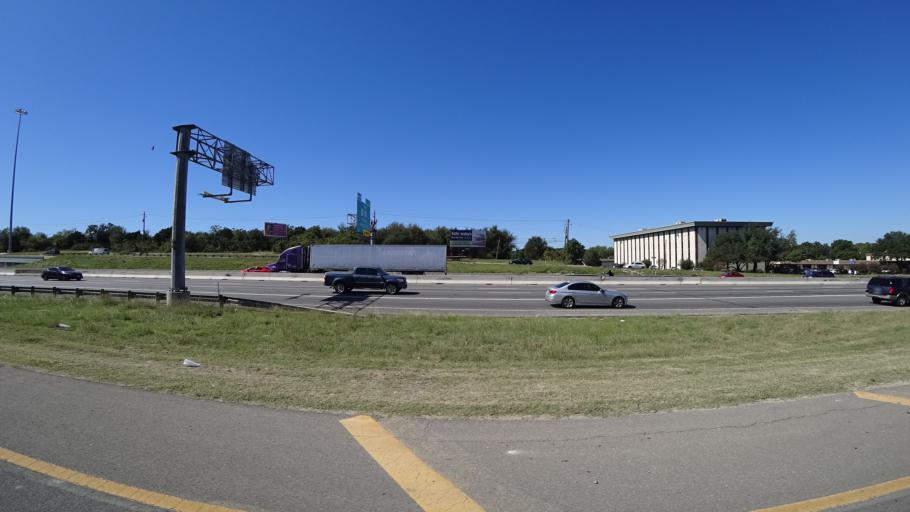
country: US
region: Texas
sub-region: Travis County
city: Austin
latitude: 30.2259
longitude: -97.7454
